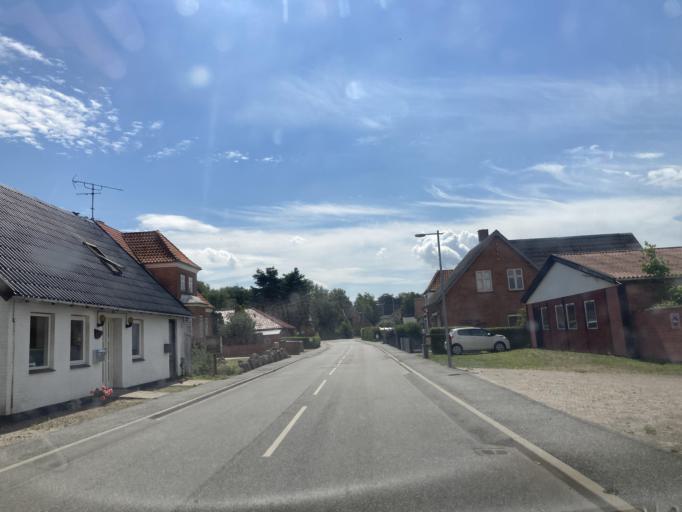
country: DK
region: Zealand
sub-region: Faxe Kommune
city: Haslev
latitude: 55.3882
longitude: 11.9386
